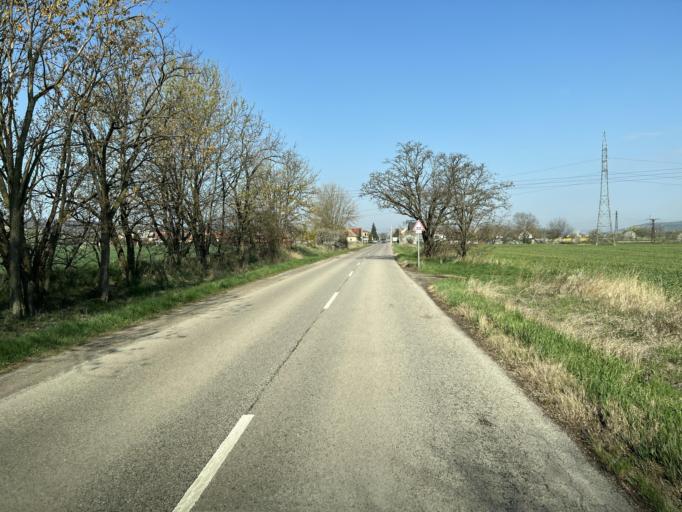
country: HU
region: Pest
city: Domony
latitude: 47.6485
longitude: 19.4488
